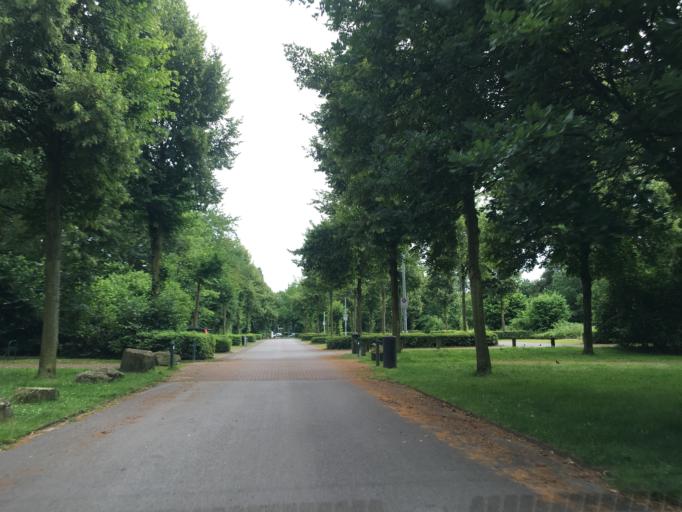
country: DE
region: North Rhine-Westphalia
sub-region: Regierungsbezirk Munster
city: Gelsenkirchen
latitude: 51.5421
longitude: 7.1091
